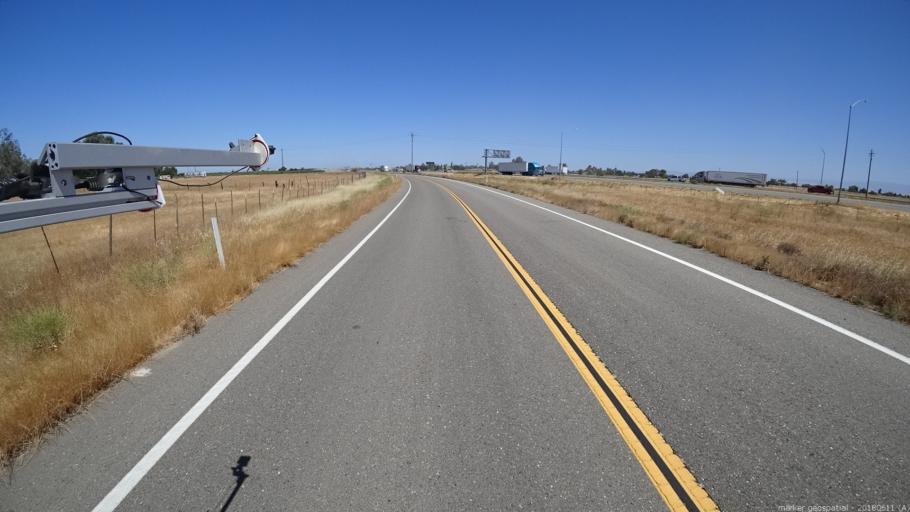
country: US
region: California
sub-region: Madera County
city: Fairmead
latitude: 37.0678
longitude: -120.1906
